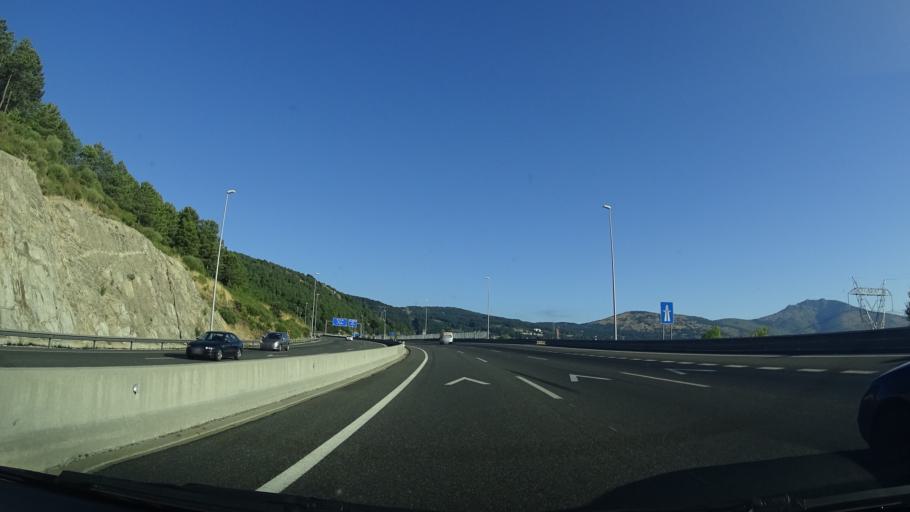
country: ES
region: Madrid
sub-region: Provincia de Madrid
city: Guadarrama
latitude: 40.6855
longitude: -4.1177
